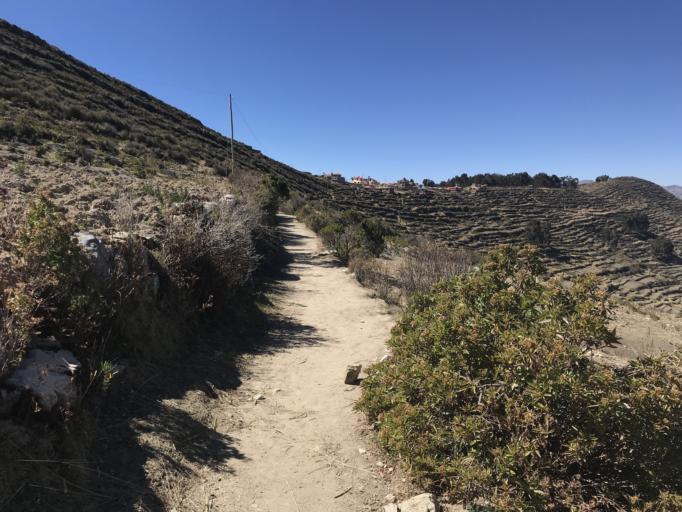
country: BO
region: La Paz
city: Yumani
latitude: -16.0333
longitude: -69.1554
